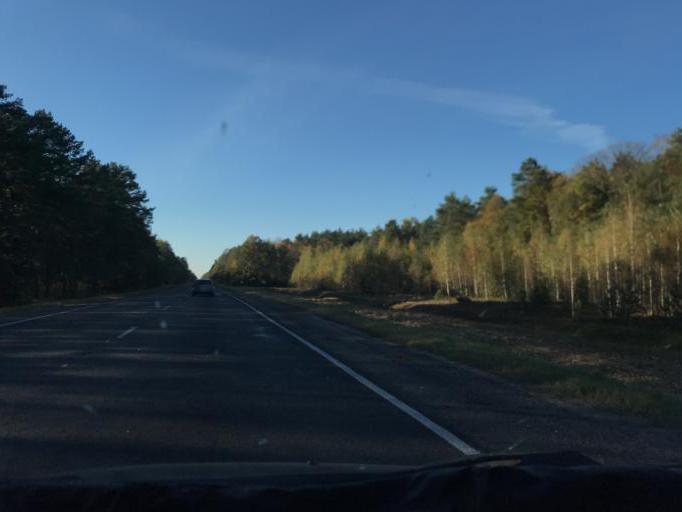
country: BY
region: Gomel
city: Kalinkavichy
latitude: 52.1686
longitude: 29.2124
